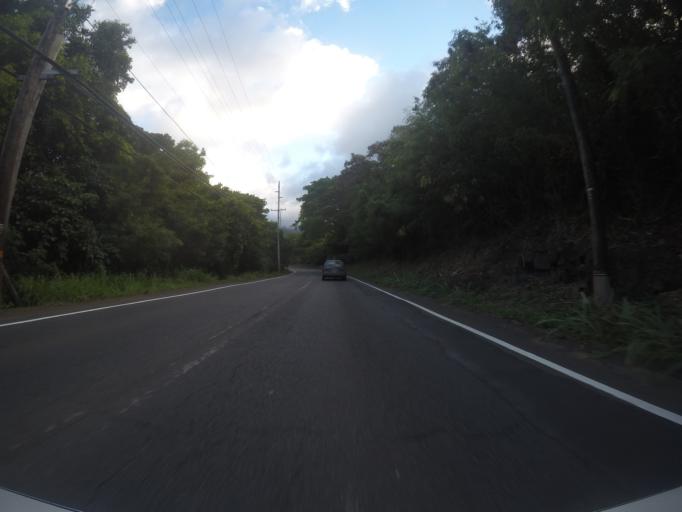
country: US
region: Hawaii
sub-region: Honolulu County
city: Ka'a'awa
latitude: 21.5154
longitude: -157.8434
